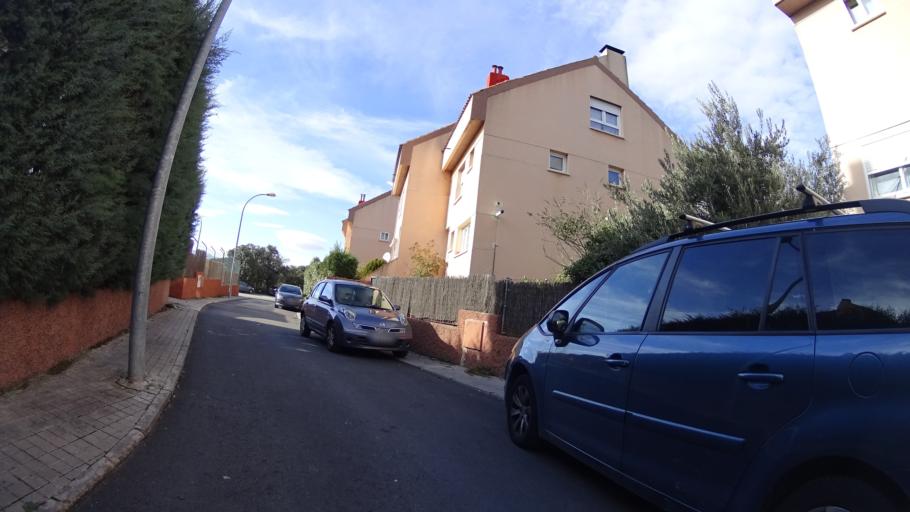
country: ES
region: Madrid
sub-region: Provincia de Madrid
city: Galapagar
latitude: 40.5808
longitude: -4.0146
